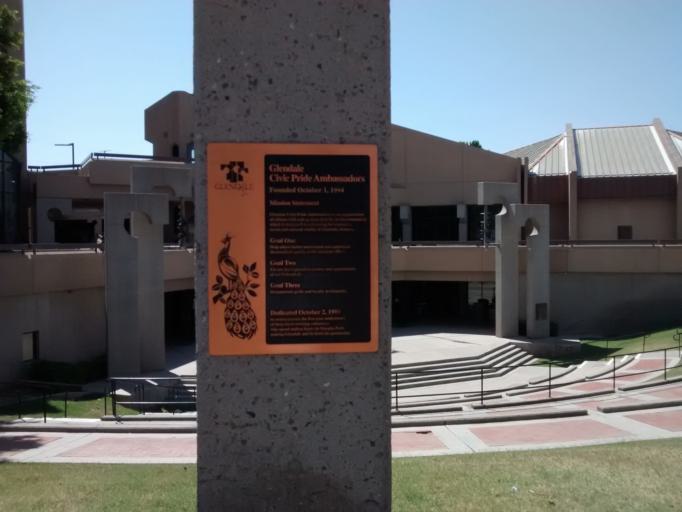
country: US
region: Arizona
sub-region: Maricopa County
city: Glendale
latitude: 33.5392
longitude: -112.1849
